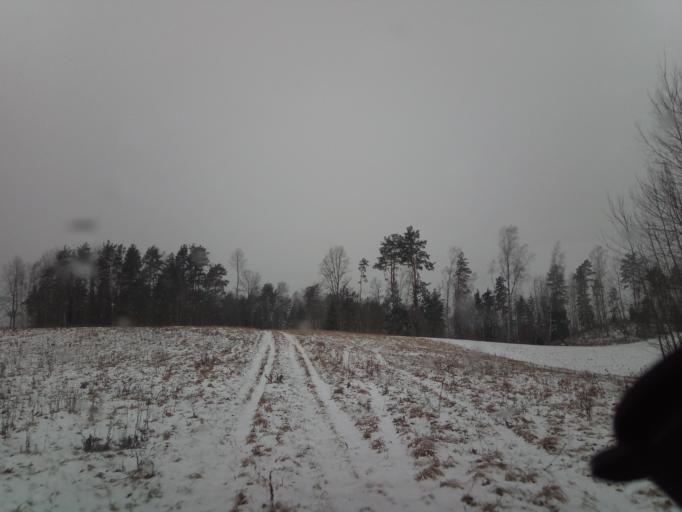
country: LT
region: Utenos apskritis
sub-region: Anyksciai
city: Anyksciai
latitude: 55.4093
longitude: 25.1948
